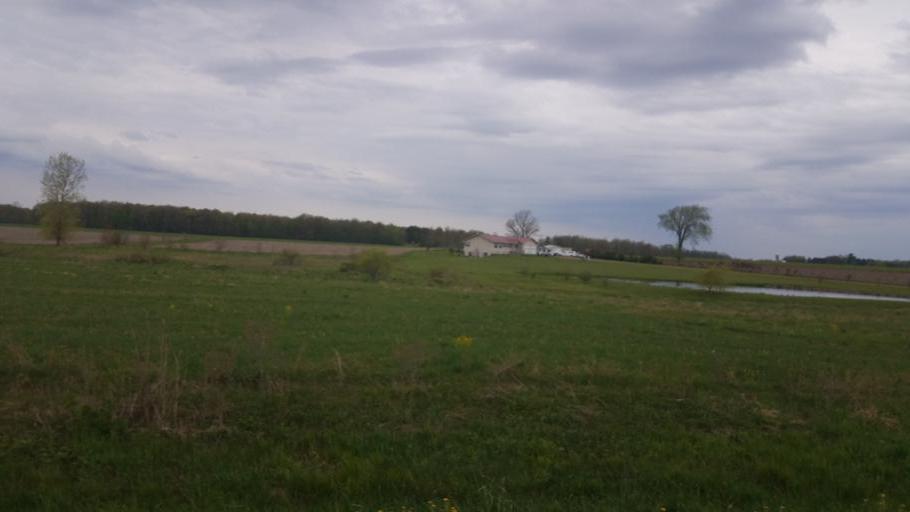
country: US
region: Wisconsin
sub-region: Marathon County
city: Spencer
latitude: 44.6469
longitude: -90.3773
